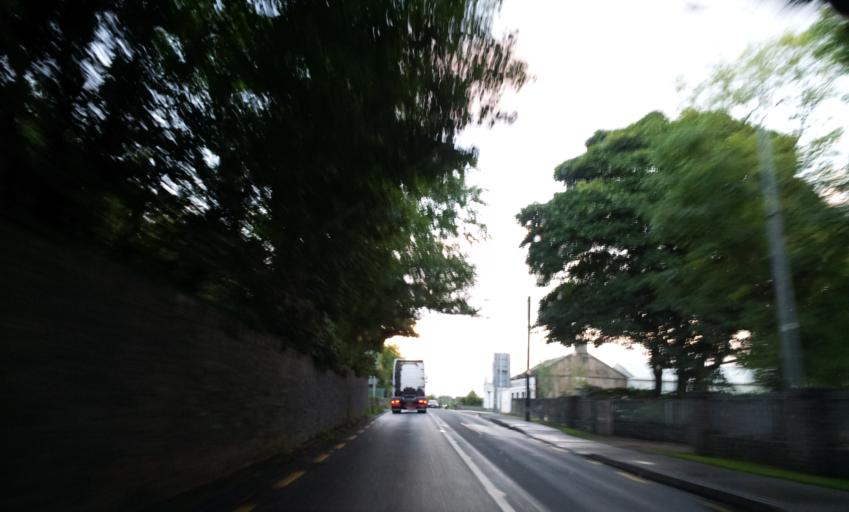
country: IE
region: Munster
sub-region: County Limerick
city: Adare
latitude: 52.5550
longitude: -8.8029
